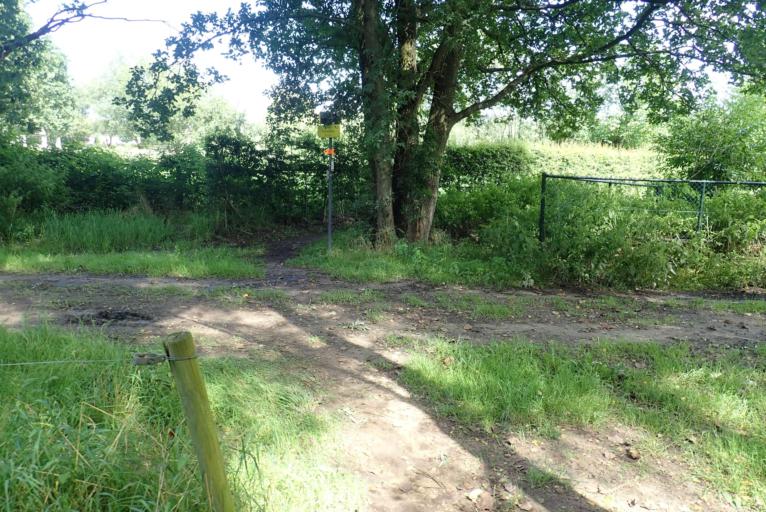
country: BE
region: Flanders
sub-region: Provincie Vlaams-Brabant
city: Begijnendijk
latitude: 50.9886
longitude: 4.7999
